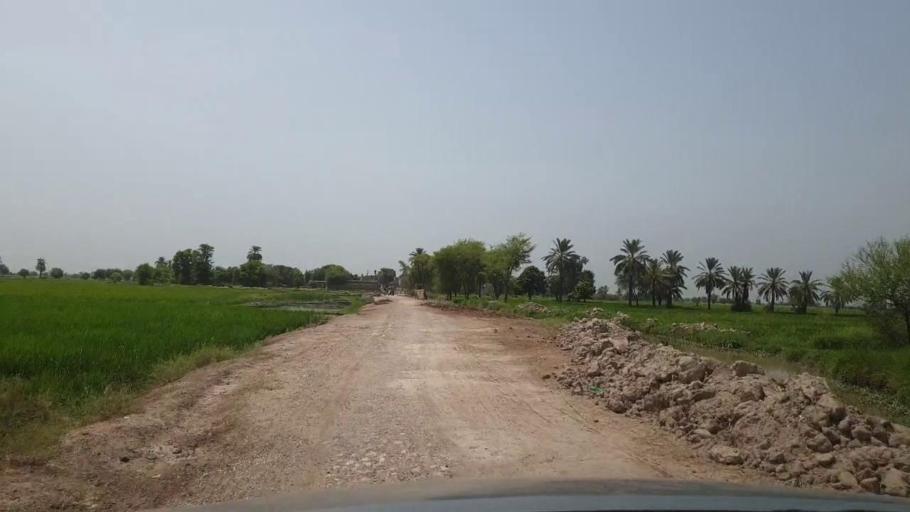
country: PK
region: Sindh
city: Madeji
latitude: 27.7896
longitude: 68.4344
